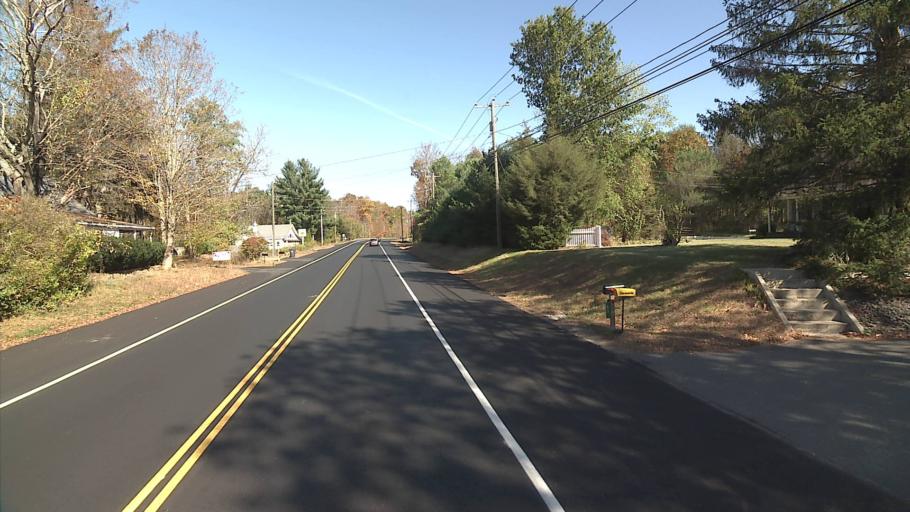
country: US
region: Connecticut
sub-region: Windham County
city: Windham
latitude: 41.7662
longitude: -72.1390
